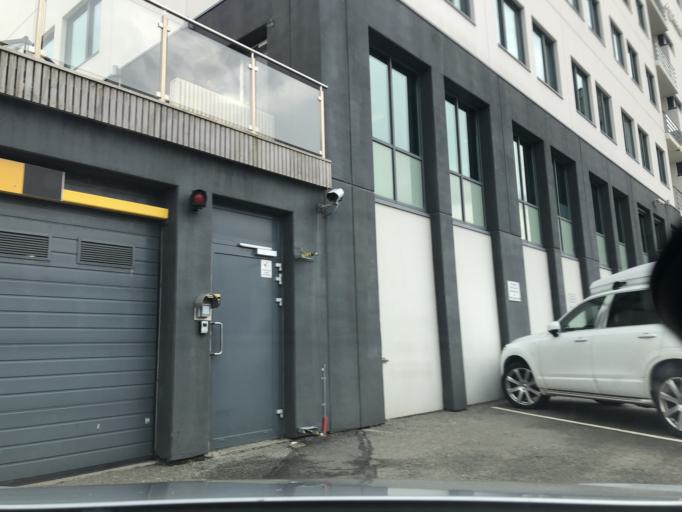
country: NO
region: Rogaland
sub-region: Stavanger
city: Stavanger
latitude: 58.9726
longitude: 5.7515
